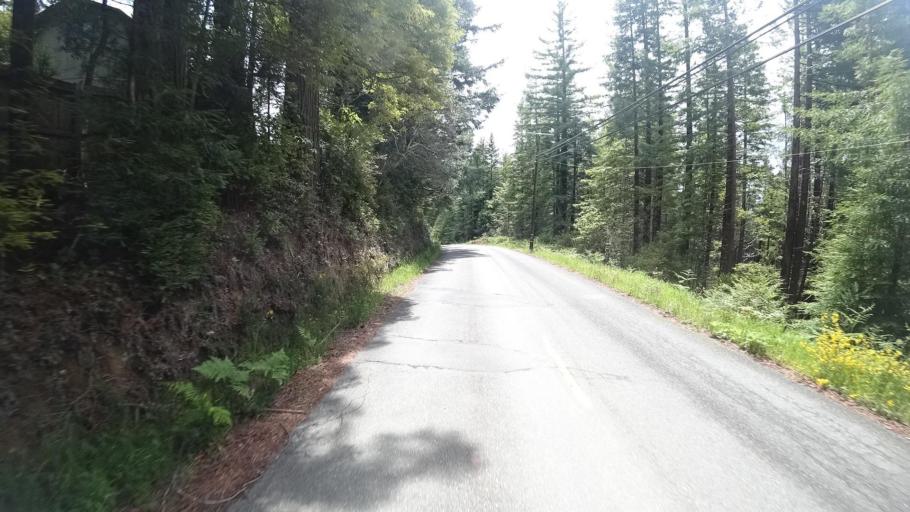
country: US
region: California
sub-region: Humboldt County
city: Bayside
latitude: 40.7940
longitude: -124.0251
